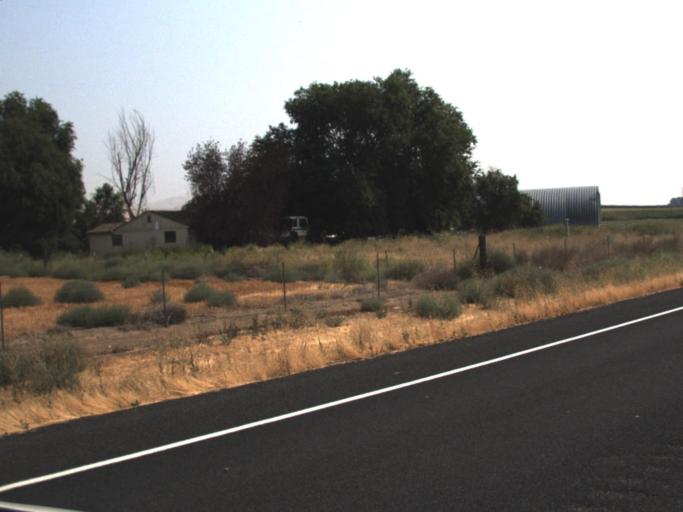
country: US
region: Washington
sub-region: Yakima County
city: Zillah
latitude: 46.5310
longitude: -120.2761
